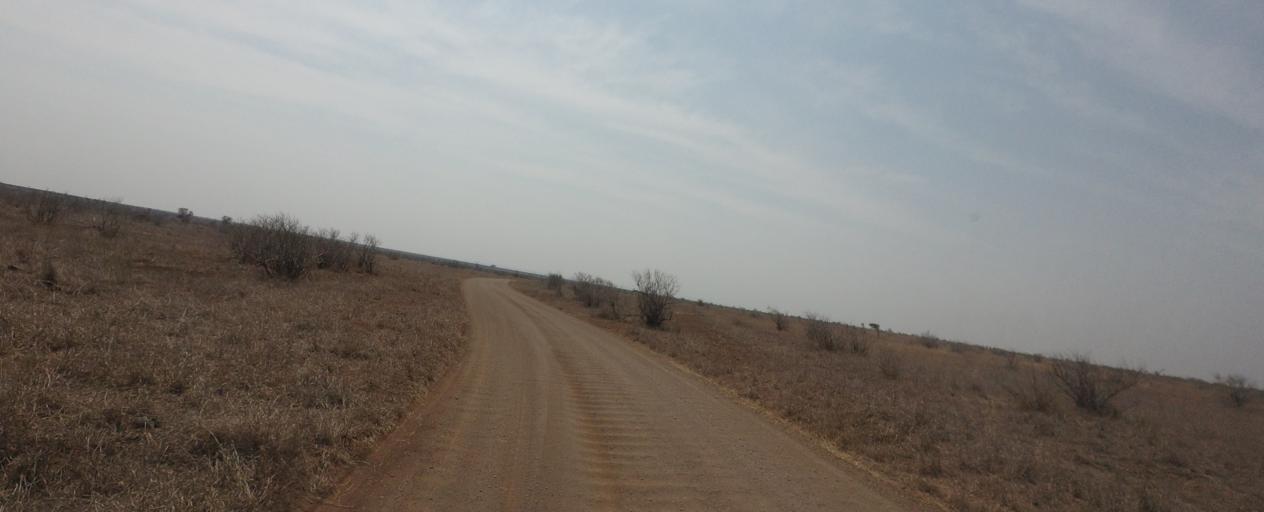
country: ZA
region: Limpopo
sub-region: Mopani District Municipality
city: Phalaborwa
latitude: -24.2542
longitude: 31.6996
